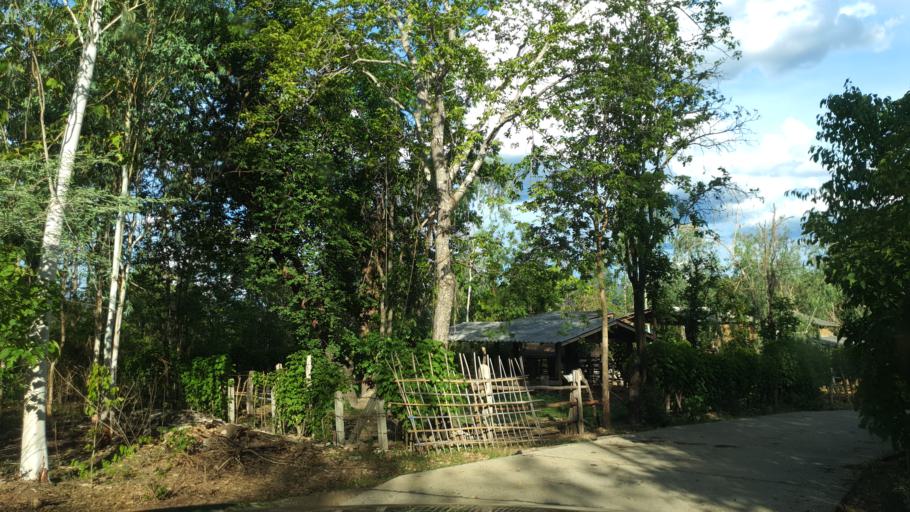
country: TH
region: Lampang
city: Sop Prap
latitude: 17.8806
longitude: 99.2966
